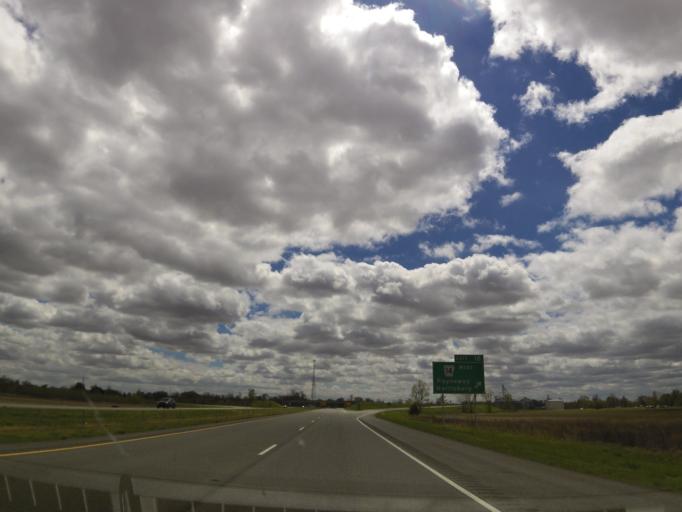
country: US
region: Arkansas
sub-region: Poinsett County
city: Marked Tree
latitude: 35.5514
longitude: -90.4970
